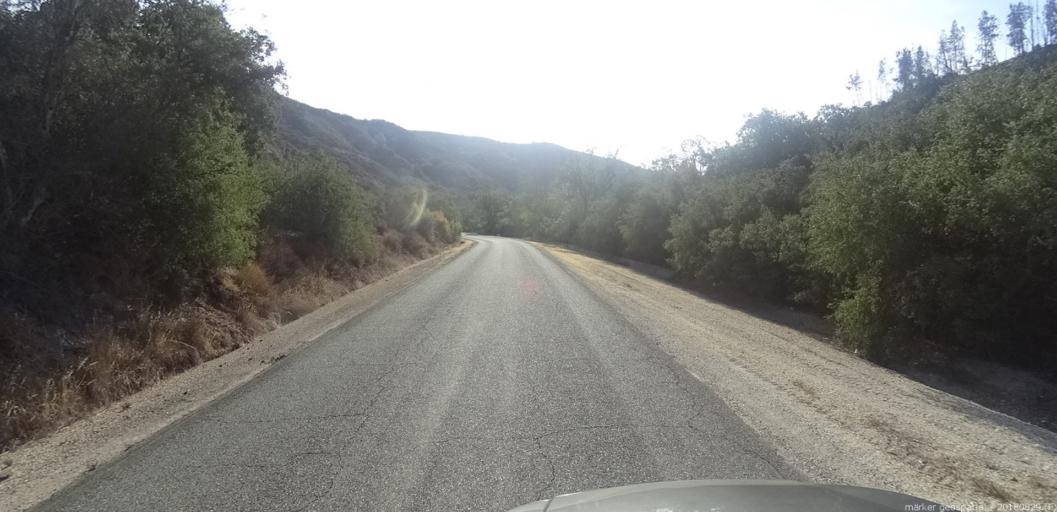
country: US
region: California
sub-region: Monterey County
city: King City
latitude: 36.0284
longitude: -121.0728
